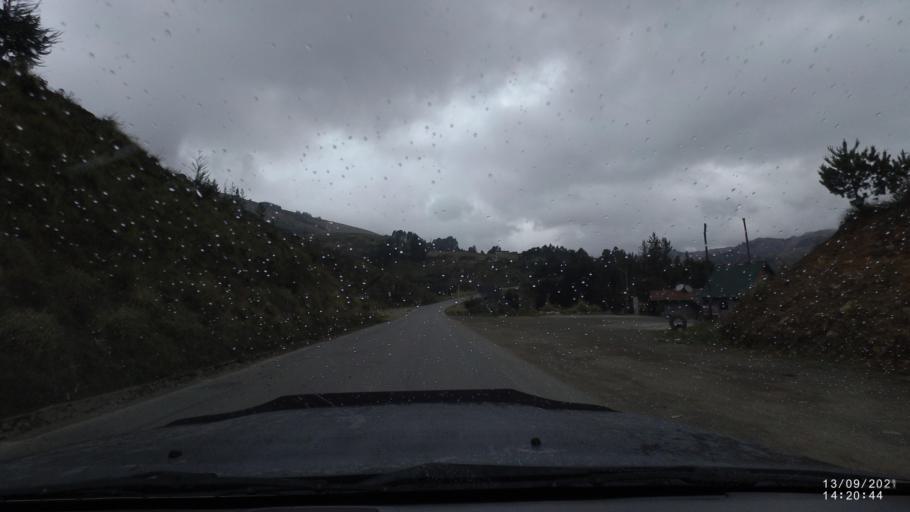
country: BO
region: Cochabamba
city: Colomi
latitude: -17.2541
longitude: -65.8935
